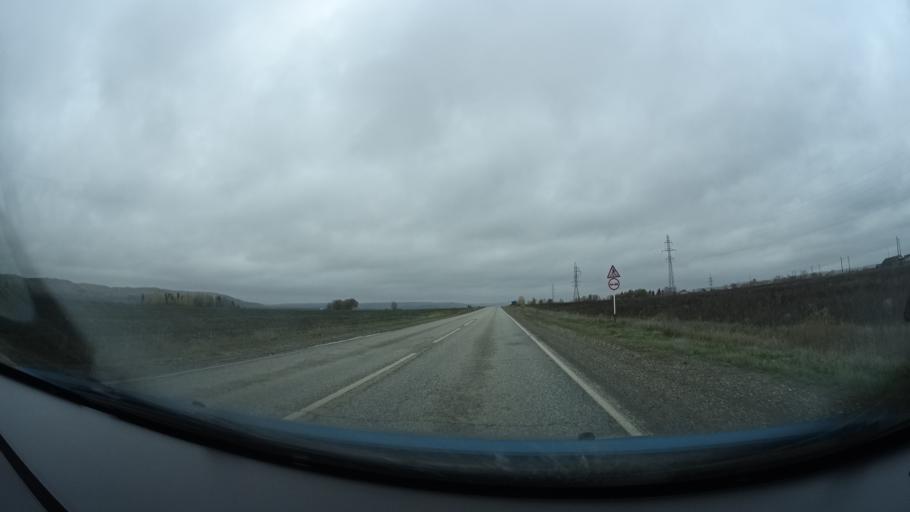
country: RU
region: Perm
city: Barda
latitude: 57.0981
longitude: 55.5310
